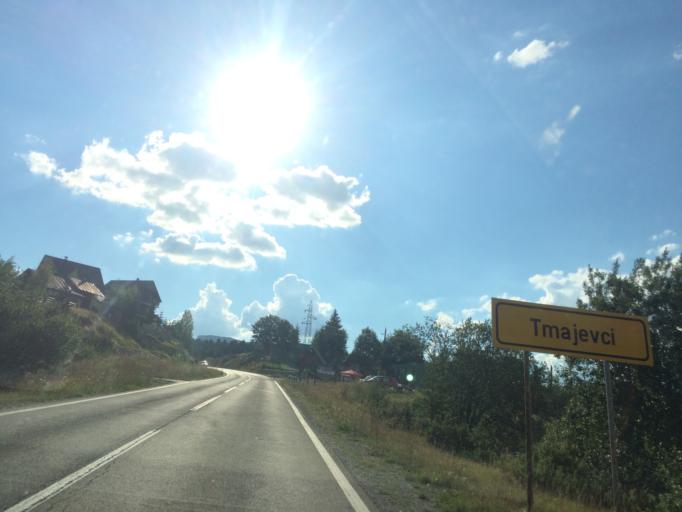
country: ME
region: Opstina Zabljak
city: Zabljak
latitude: 43.1631
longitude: 19.1421
